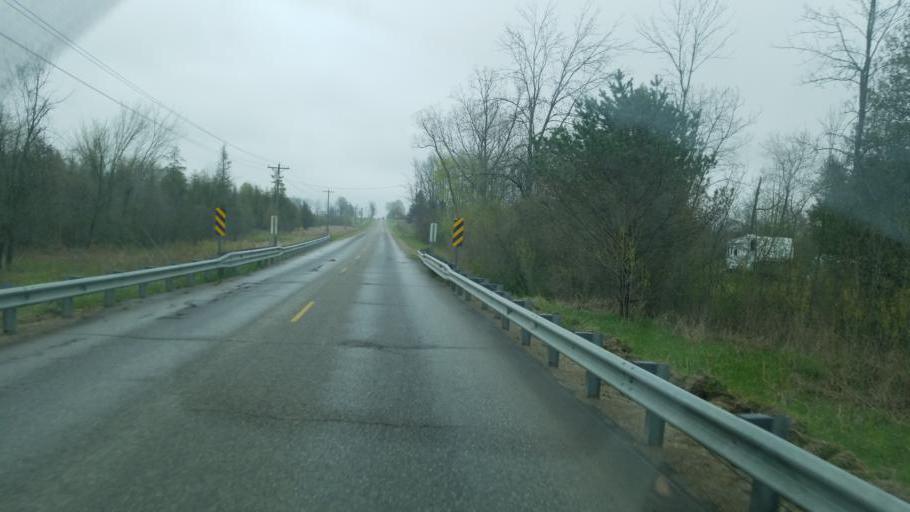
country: US
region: Michigan
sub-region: Mecosta County
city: Canadian Lakes
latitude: 43.5424
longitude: -85.3779
